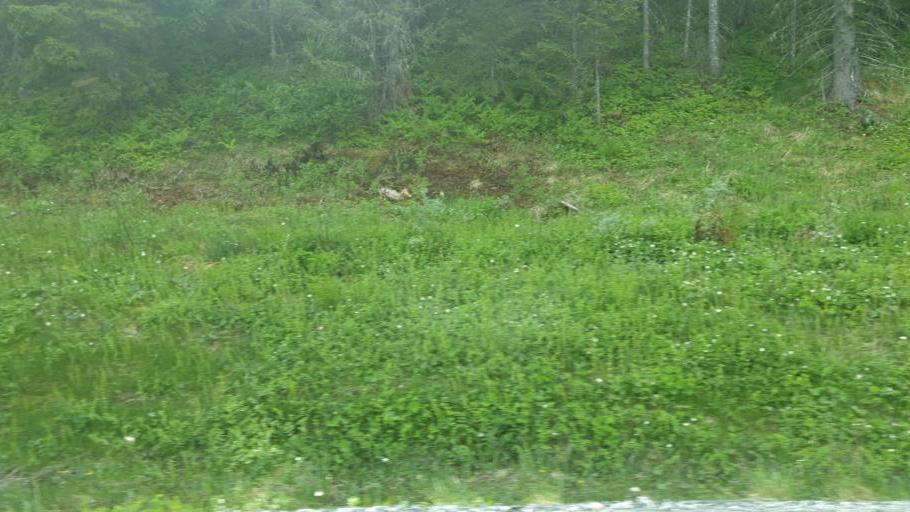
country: NO
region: Nord-Trondelag
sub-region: Leksvik
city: Leksvik
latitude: 63.6901
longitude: 10.5222
